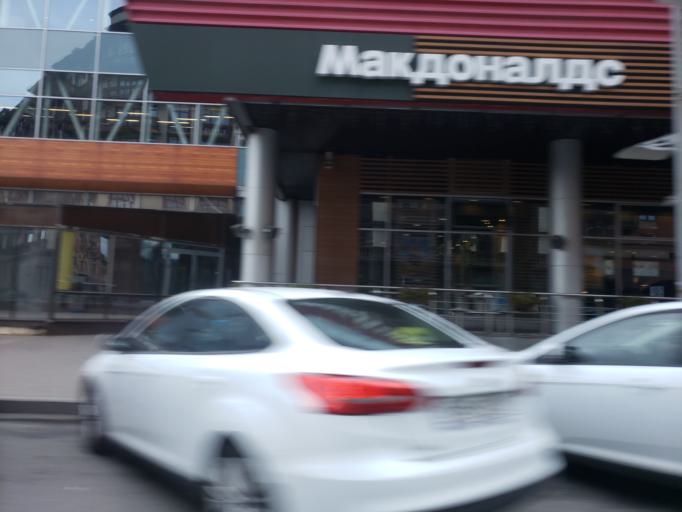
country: RU
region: St.-Petersburg
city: Vasyl'evsky Ostrov
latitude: 59.9388
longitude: 30.2300
